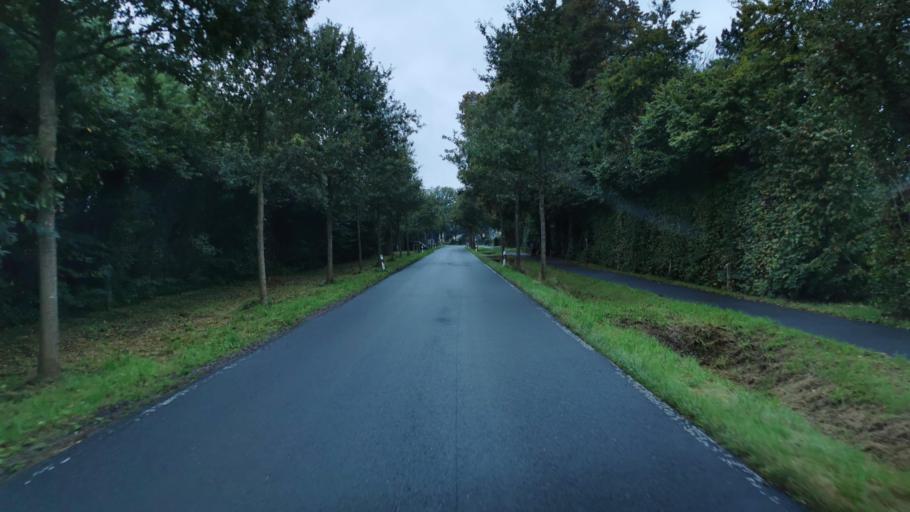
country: DE
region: North Rhine-Westphalia
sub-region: Regierungsbezirk Munster
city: Vreden
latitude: 52.0111
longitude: 6.7910
